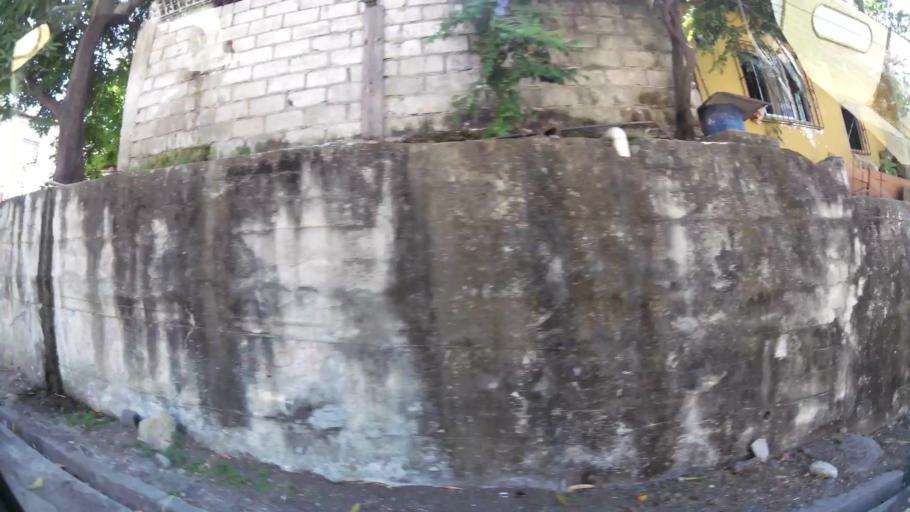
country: EC
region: Guayas
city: Eloy Alfaro
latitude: -2.1296
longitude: -79.9153
